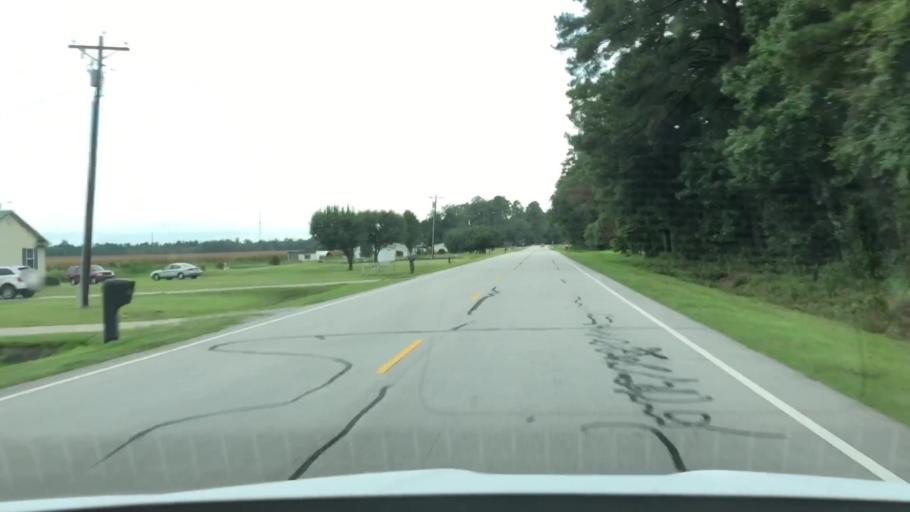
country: US
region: North Carolina
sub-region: Lenoir County
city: Kinston
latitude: 35.1176
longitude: -77.5136
